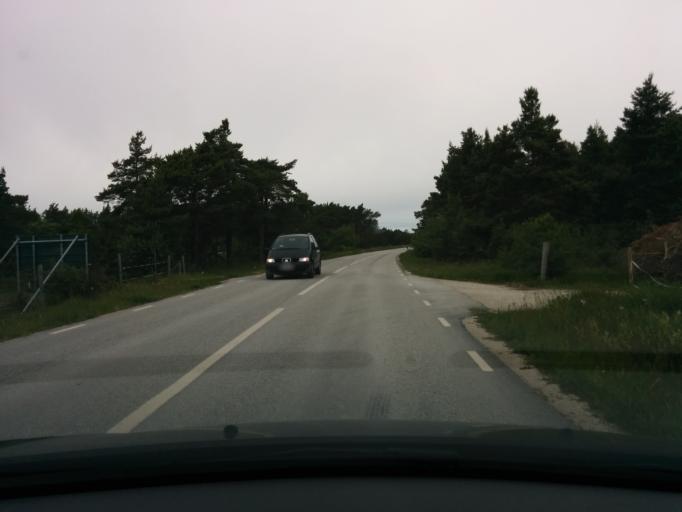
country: SE
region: Gotland
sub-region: Gotland
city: Slite
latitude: 57.6760
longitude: 18.7696
